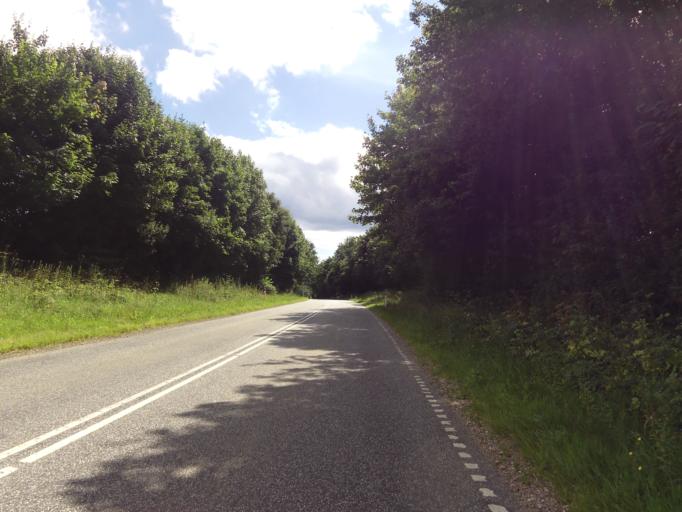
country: DK
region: South Denmark
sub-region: Haderslev Kommune
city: Haderslev
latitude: 55.2703
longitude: 9.4271
